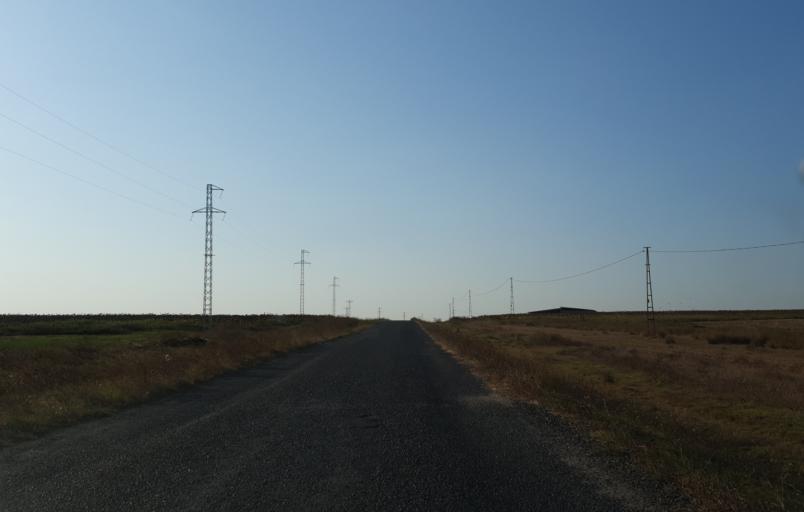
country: TR
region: Tekirdag
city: Beyazkoy
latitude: 41.3966
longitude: 27.7626
